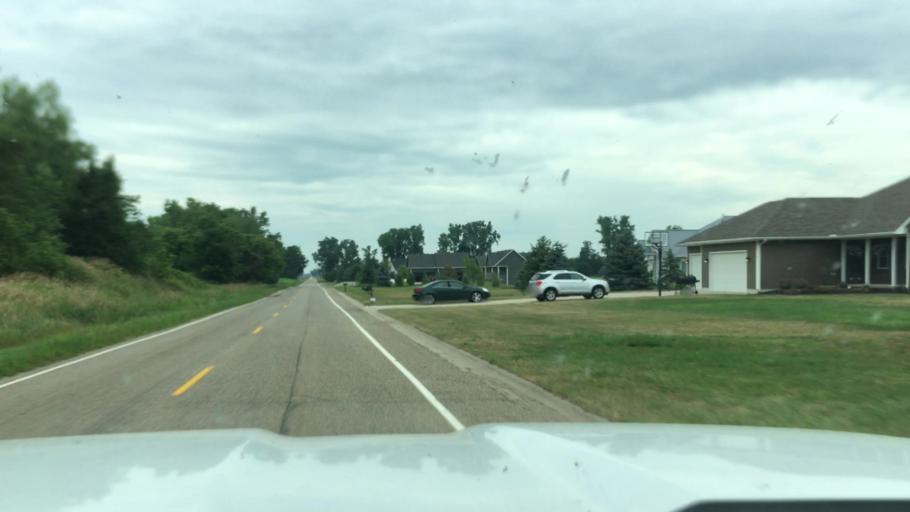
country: US
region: Michigan
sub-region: Clinton County
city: Saint Johns
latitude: 43.0493
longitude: -84.4841
